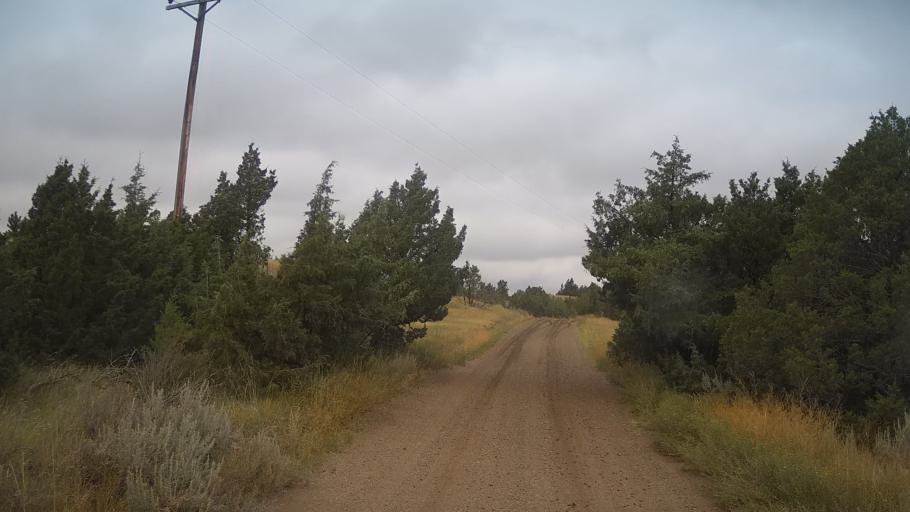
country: US
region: Montana
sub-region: Dawson County
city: Glendive
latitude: 47.0432
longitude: -104.6754
